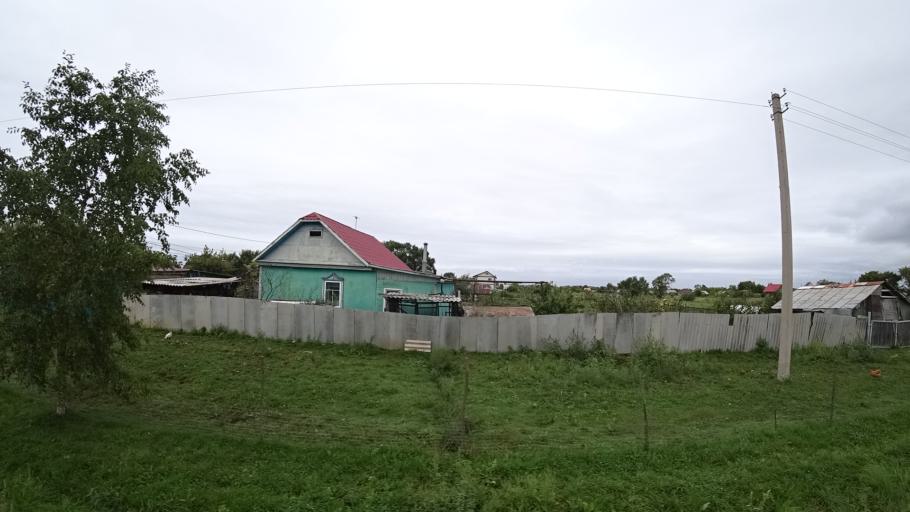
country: RU
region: Primorskiy
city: Chernigovka
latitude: 44.3389
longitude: 132.5616
